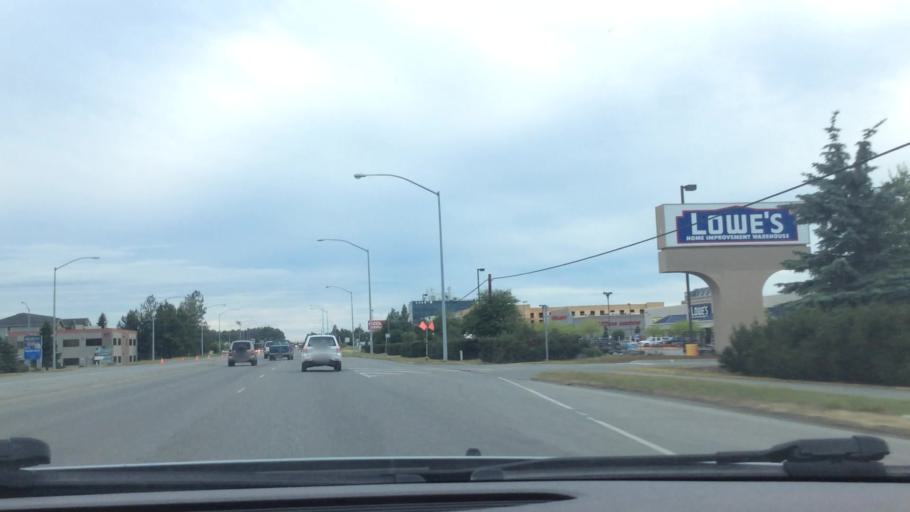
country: US
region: Alaska
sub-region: Anchorage Municipality
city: Anchorage
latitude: 61.1795
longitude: -149.8761
